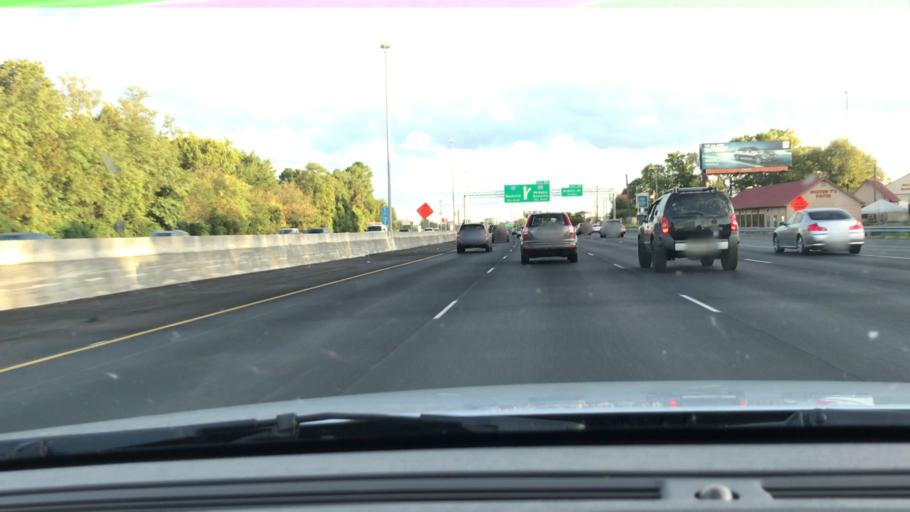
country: US
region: Tennessee
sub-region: Davidson County
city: Oak Hill
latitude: 36.0900
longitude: -86.7626
